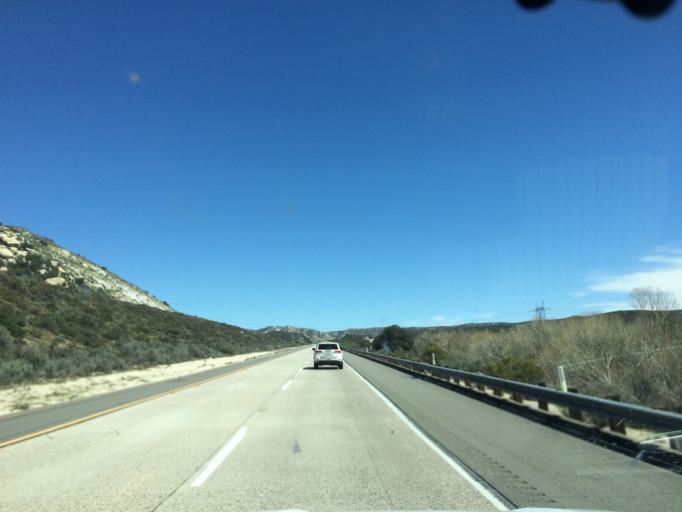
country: US
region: California
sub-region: San Diego County
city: Campo
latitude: 32.7249
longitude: -116.4392
